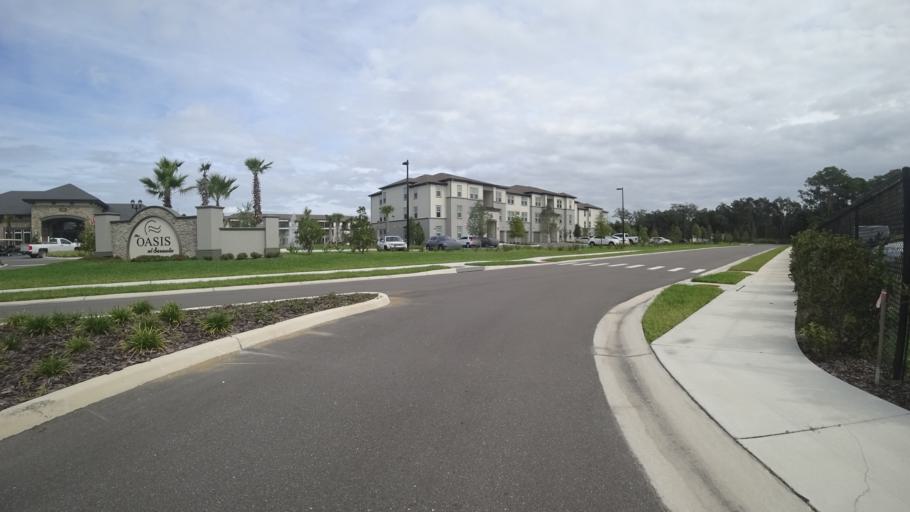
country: US
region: Florida
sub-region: Sarasota County
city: North Sarasota
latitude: 27.3906
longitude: -82.5277
